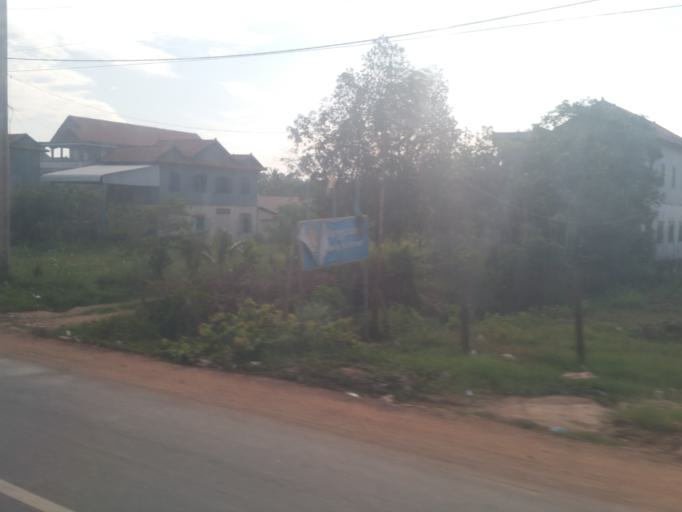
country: KH
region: Phnom Penh
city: Phnom Penh
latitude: 11.6665
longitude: 104.9133
